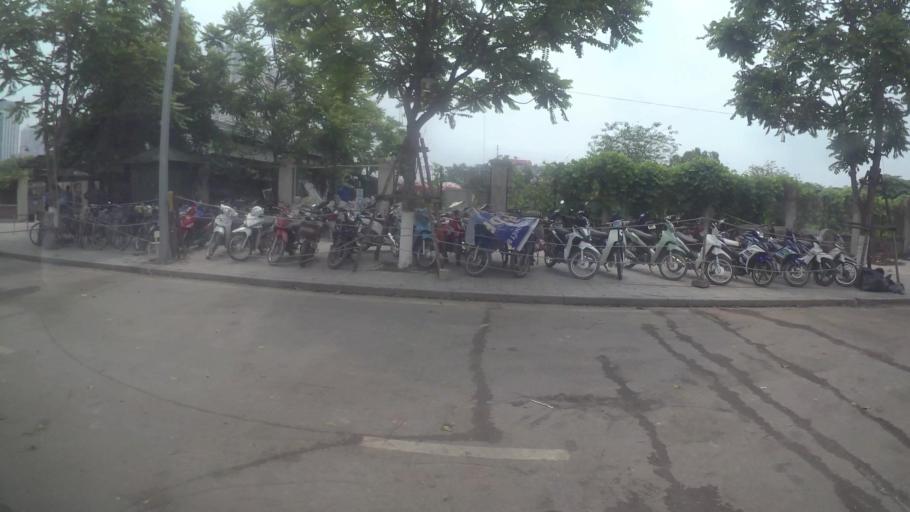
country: VN
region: Ha Noi
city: Ha Dong
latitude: 20.9733
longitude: 105.7531
